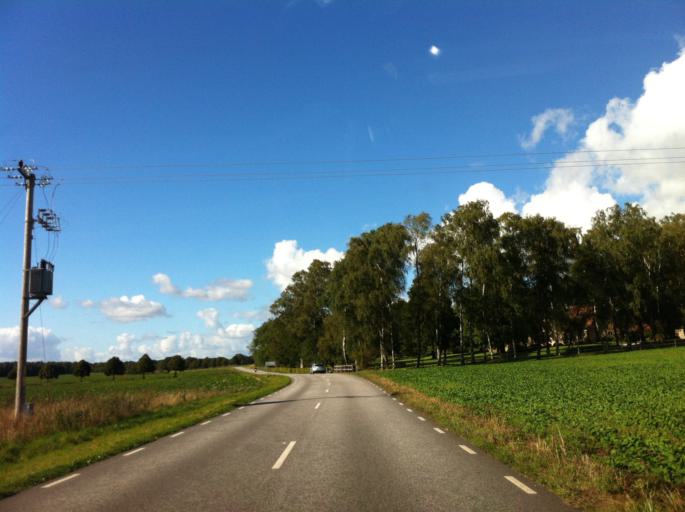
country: SE
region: Skane
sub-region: Sjobo Kommun
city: Sjoebo
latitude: 55.6763
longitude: 13.6575
